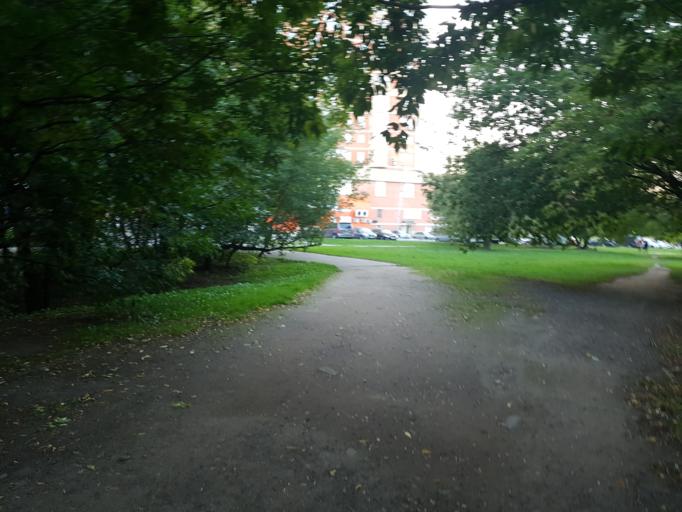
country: RU
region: Moscow
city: Solntsevo
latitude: 55.6506
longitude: 37.3895
